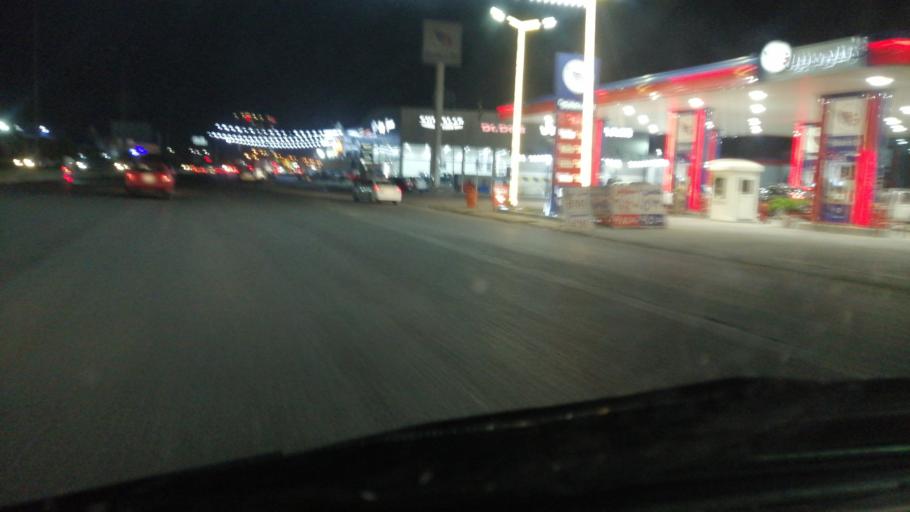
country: IQ
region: Arbil
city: Erbil
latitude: 36.1570
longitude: 43.9894
